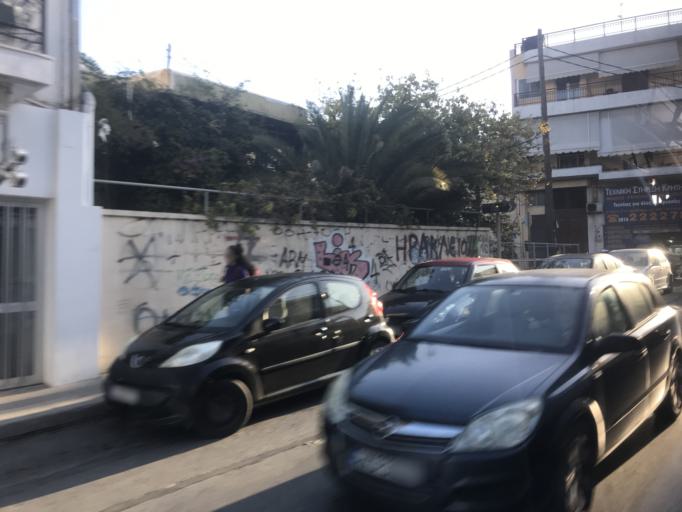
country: GR
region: Crete
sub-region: Nomos Irakleiou
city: Irakleion
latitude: 35.3387
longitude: 25.1461
